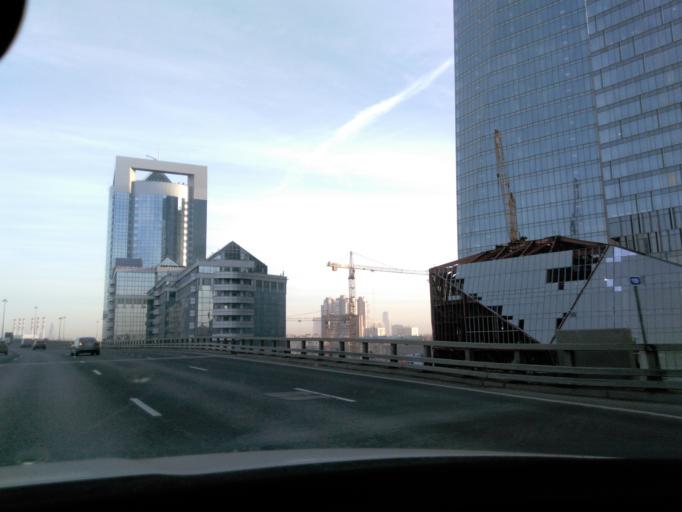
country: RU
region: Moskovskaya
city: Presnenskiy
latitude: 55.7488
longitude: 37.5324
